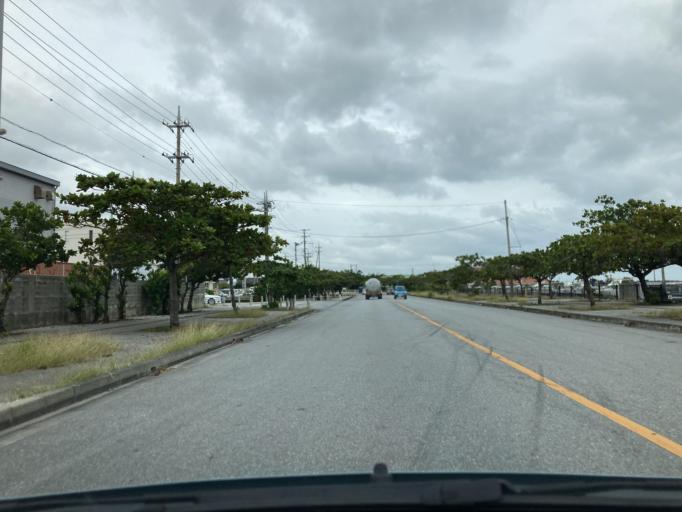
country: JP
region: Okinawa
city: Ginowan
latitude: 26.2178
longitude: 127.7767
